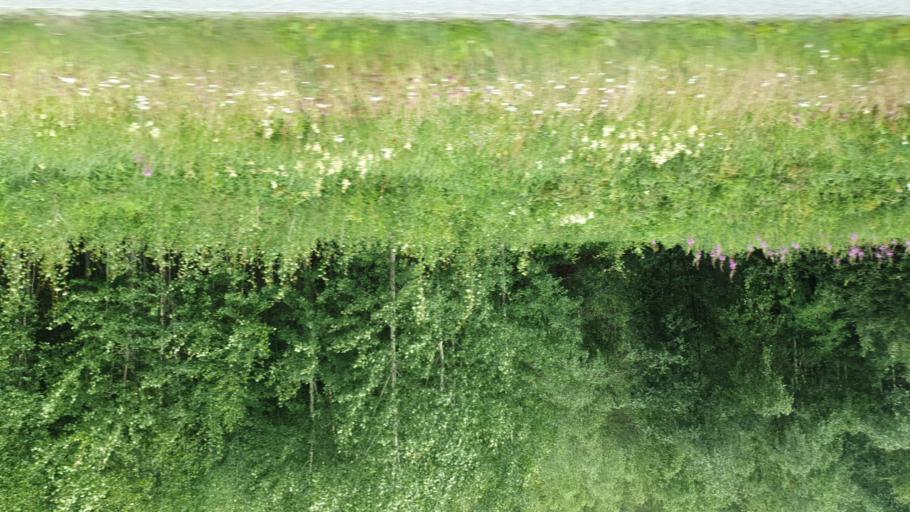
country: NO
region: Oppland
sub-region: Sel
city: Otta
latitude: 61.8436
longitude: 9.3820
